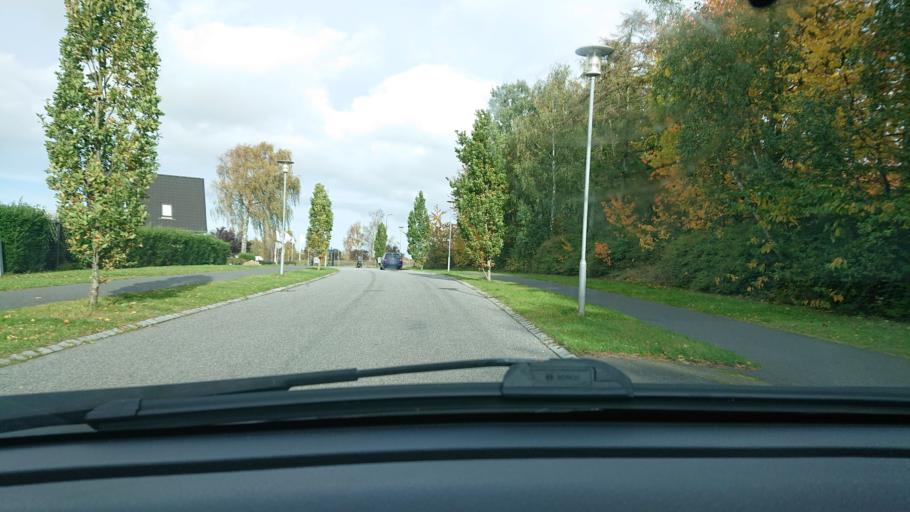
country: DK
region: South Denmark
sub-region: Nyborg Kommune
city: Nyborg
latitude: 55.3084
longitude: 10.7609
